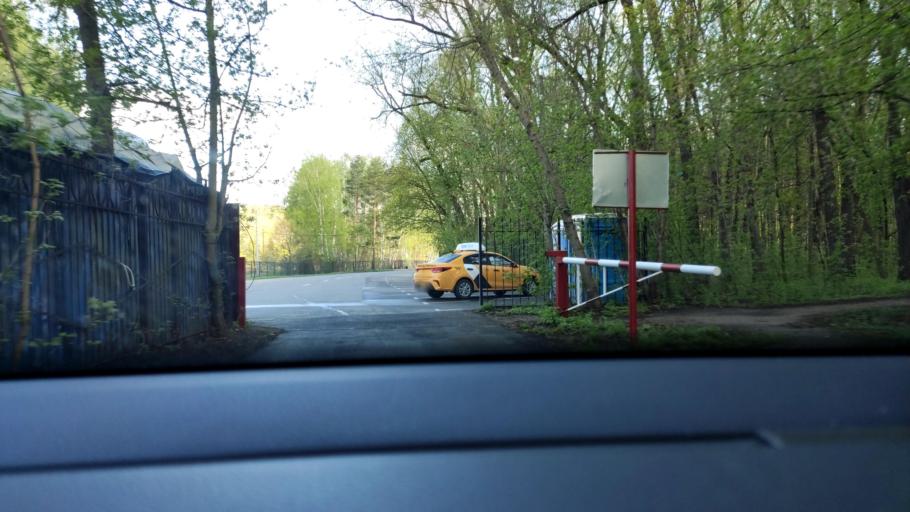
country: RU
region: Moscow
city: Strogino
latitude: 55.7787
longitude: 37.4072
